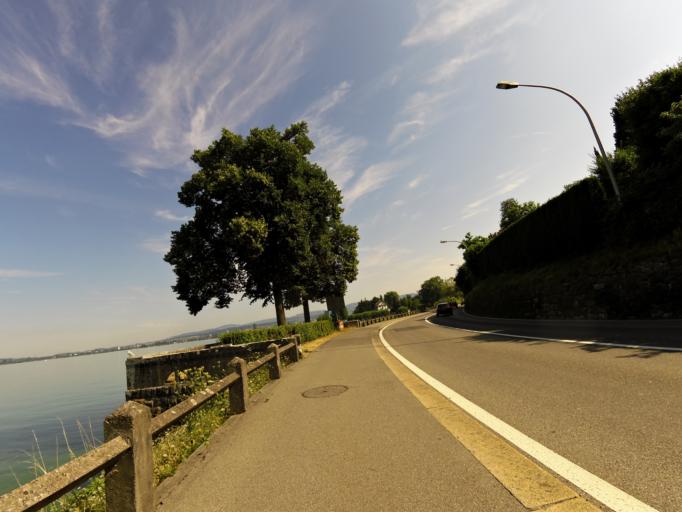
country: CH
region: Zug
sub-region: Zug
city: Zug
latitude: 47.1519
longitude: 8.5088
